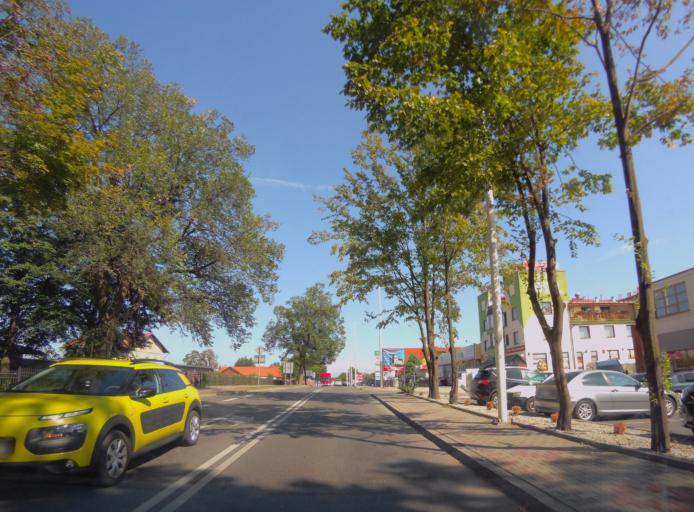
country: PL
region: Subcarpathian Voivodeship
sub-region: Powiat lezajski
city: Lezajsk
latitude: 50.2686
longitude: 22.4094
